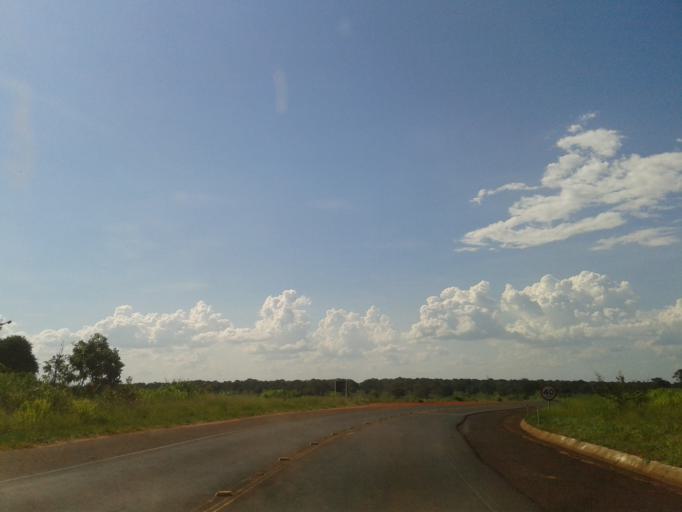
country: BR
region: Minas Gerais
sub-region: Santa Vitoria
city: Santa Vitoria
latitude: -19.0431
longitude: -50.4101
